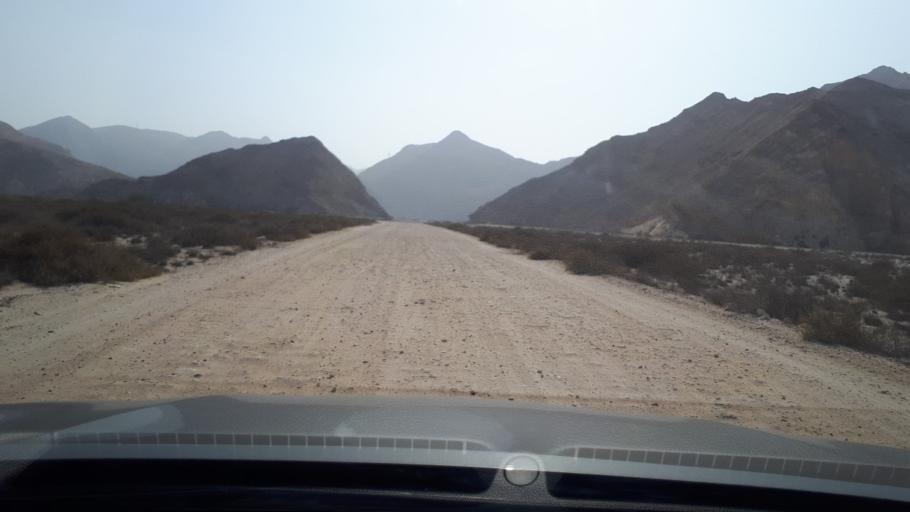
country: OM
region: Muhafazat Masqat
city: Muscat
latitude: 23.5408
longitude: 58.6674
